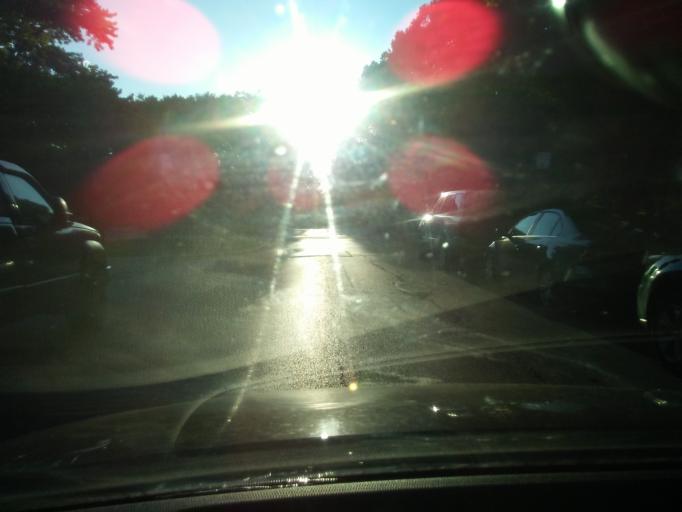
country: US
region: Illinois
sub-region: Cook County
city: Evanston
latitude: 41.9753
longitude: -87.6522
